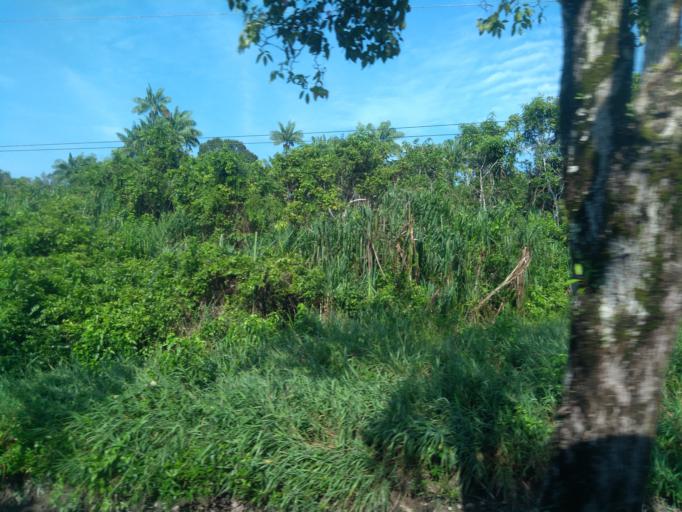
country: MY
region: Sarawak
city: Kuching
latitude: 1.6524
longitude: 110.4449
